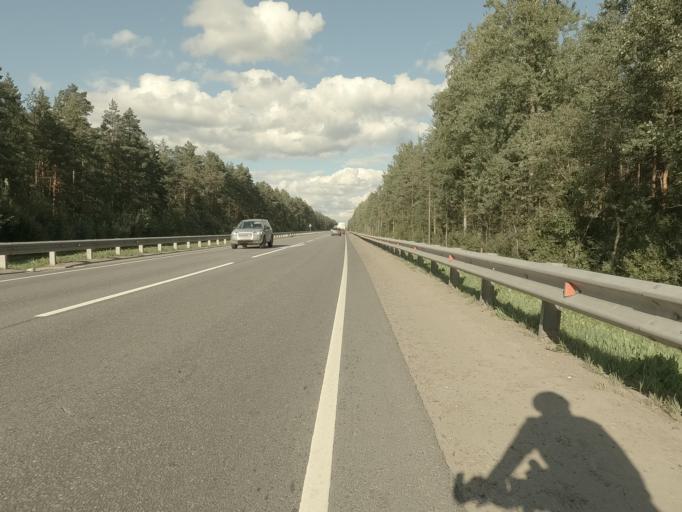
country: RU
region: Leningrad
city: Ul'yanovka
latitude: 59.6296
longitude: 30.8077
